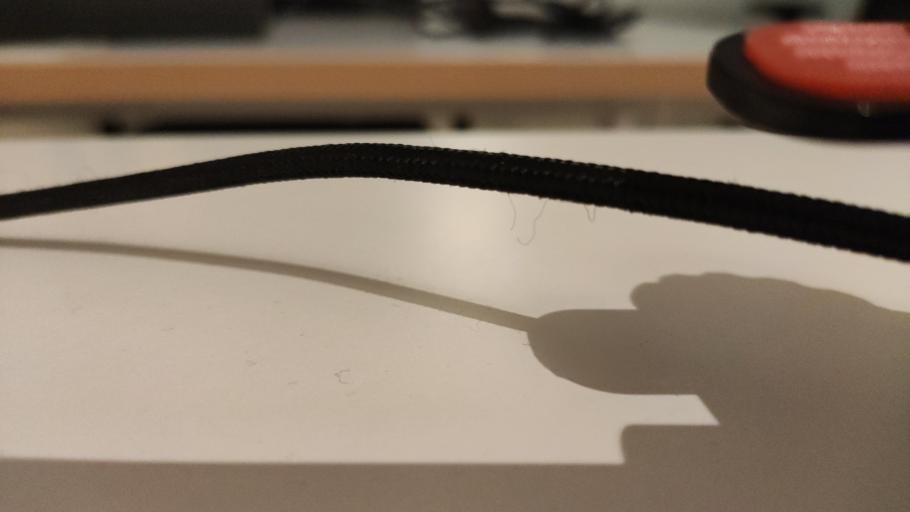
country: RU
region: Moskovskaya
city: Il'inskiy Pogost
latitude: 55.5007
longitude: 38.8734
